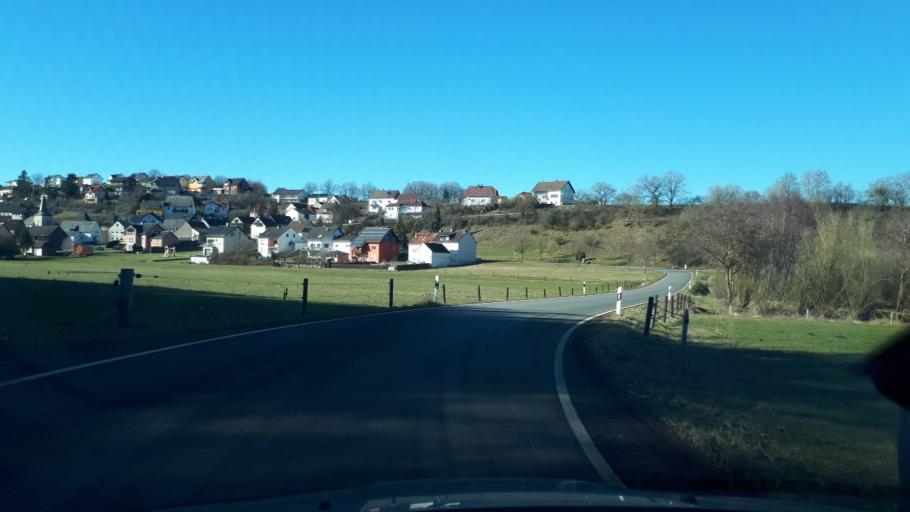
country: DE
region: Rheinland-Pfalz
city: Udler
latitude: 50.1374
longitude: 6.8812
